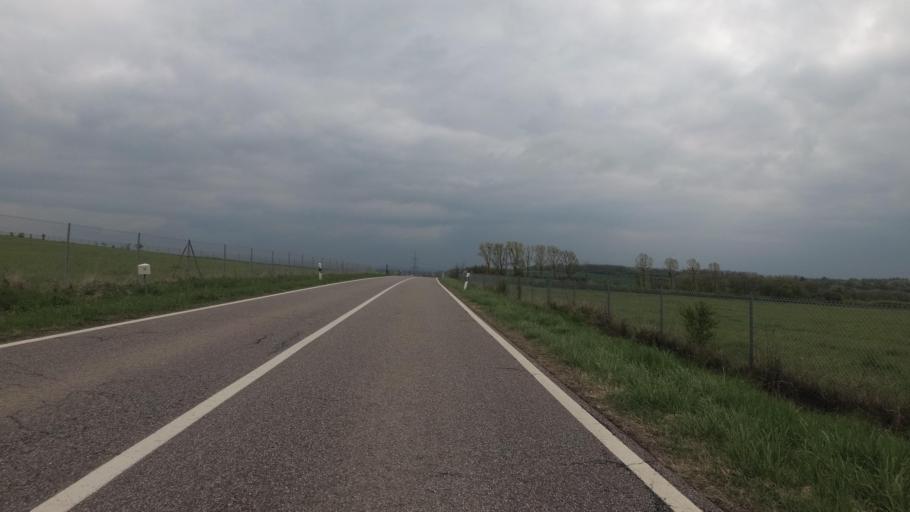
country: FR
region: Lorraine
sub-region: Departement de la Moselle
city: Merten
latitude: 49.2784
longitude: 6.6784
